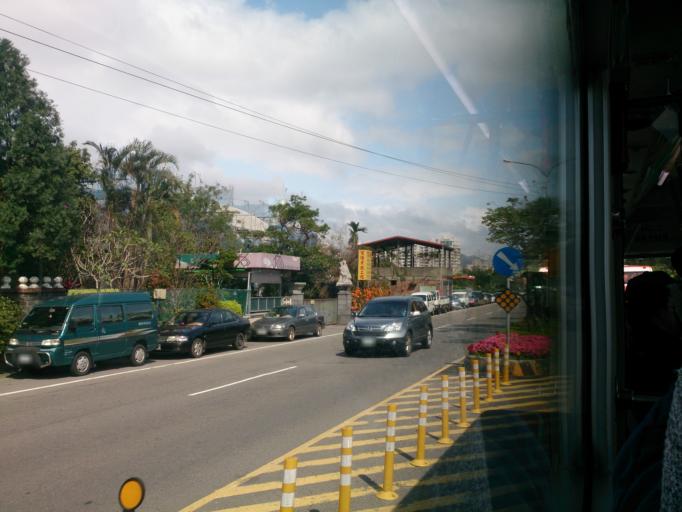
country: TW
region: Taipei
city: Taipei
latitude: 24.9984
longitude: 121.6139
